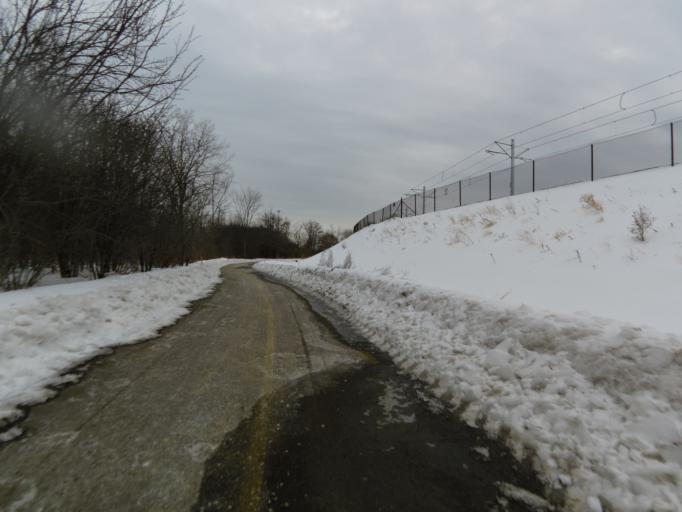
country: CA
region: Ontario
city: Ottawa
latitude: 45.4151
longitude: -75.6602
